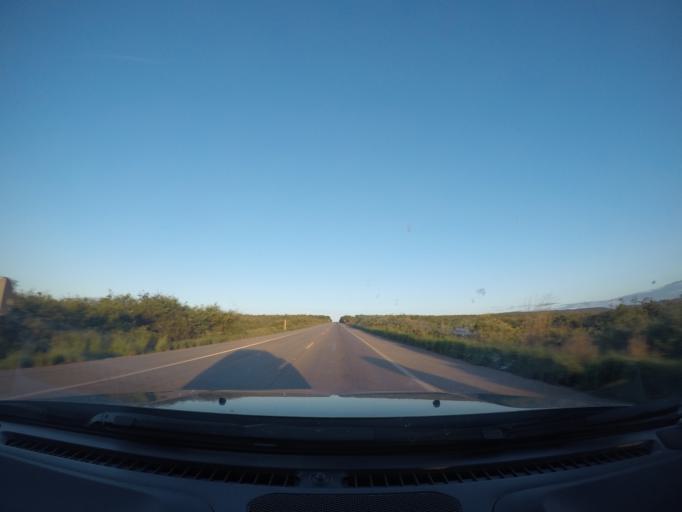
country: BR
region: Bahia
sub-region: Seabra
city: Seabra
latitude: -12.3921
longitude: -41.9155
